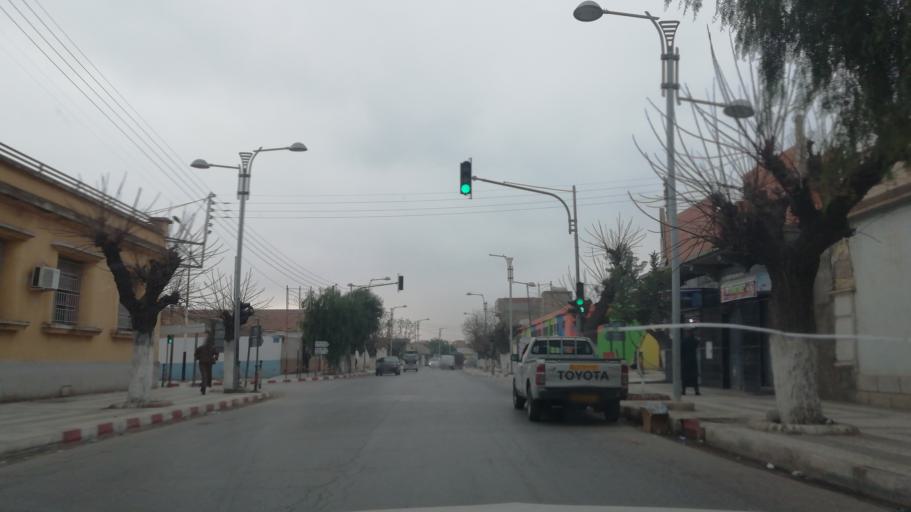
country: DZ
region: Sidi Bel Abbes
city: Sfizef
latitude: 35.2337
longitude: -0.2447
